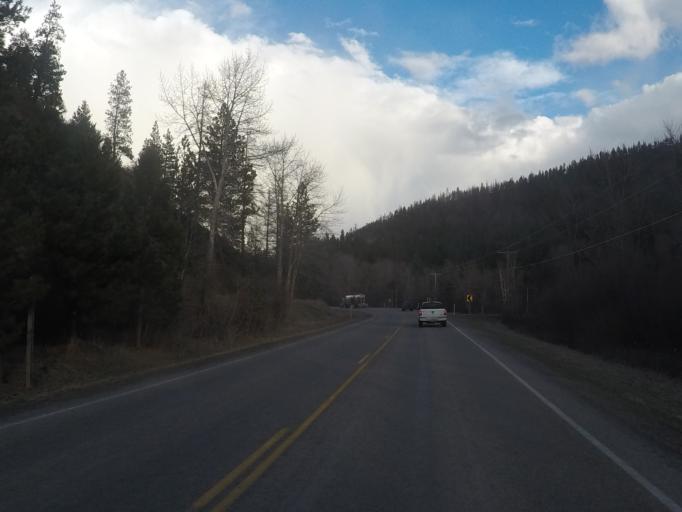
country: US
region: Montana
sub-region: Missoula County
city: Lolo
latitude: 46.7435
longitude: -114.1542
